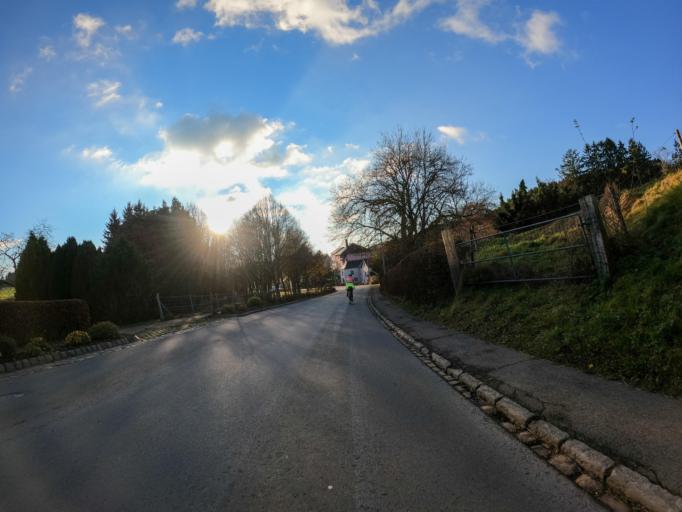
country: LU
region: Diekirch
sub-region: Canton de Wiltz
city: Bavigne
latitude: 49.9683
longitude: 5.8329
